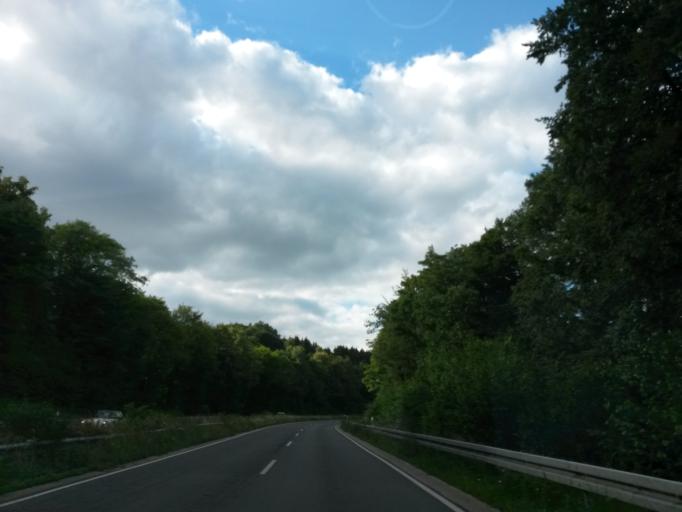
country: DE
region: North Rhine-Westphalia
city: Waldbrol
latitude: 50.9431
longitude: 7.6378
